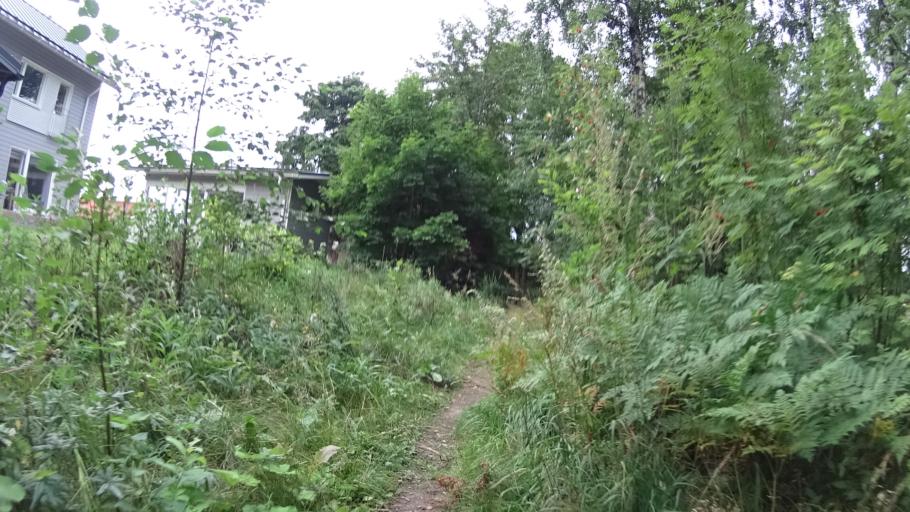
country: FI
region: Uusimaa
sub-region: Helsinki
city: Teekkarikylae
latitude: 60.2324
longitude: 24.8374
